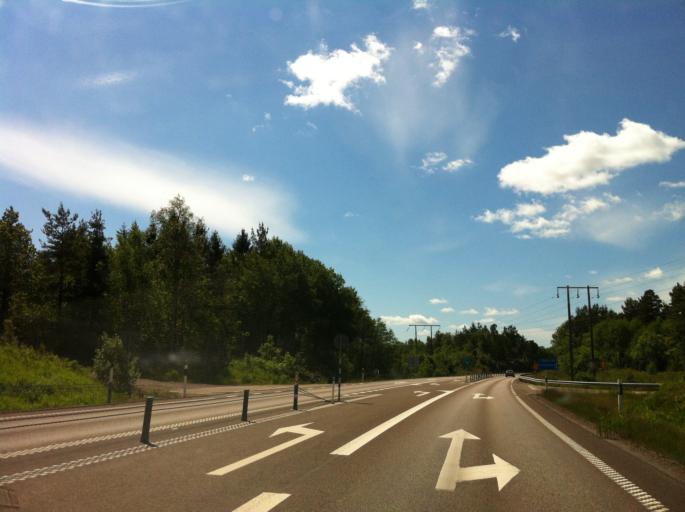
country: SE
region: Vaestra Goetaland
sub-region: Melleruds Kommun
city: Mellerud
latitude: 58.7856
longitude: 12.5136
